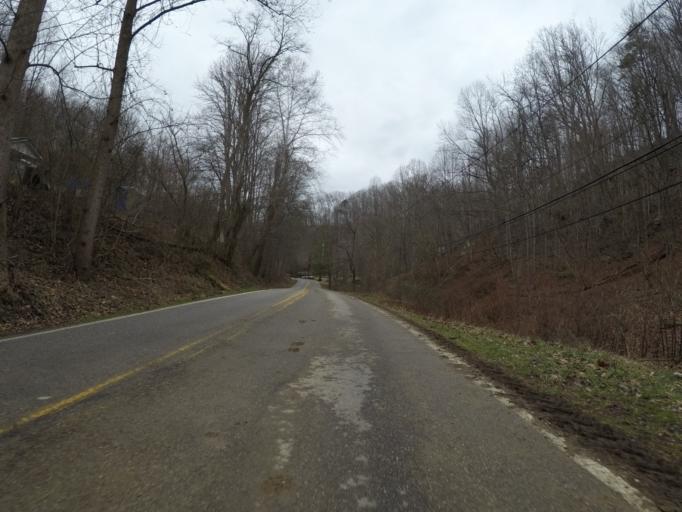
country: US
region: West Virginia
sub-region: Cabell County
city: Lesage
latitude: 38.4596
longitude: -82.2701
